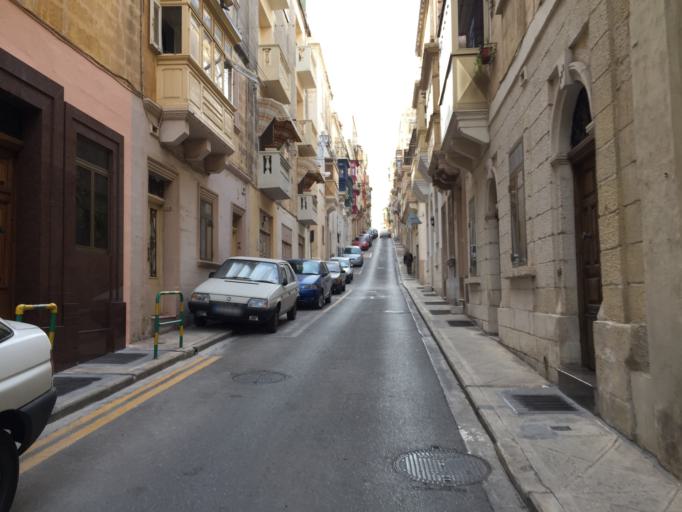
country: MT
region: L-Isla
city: Senglea
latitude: 35.8884
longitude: 14.5168
